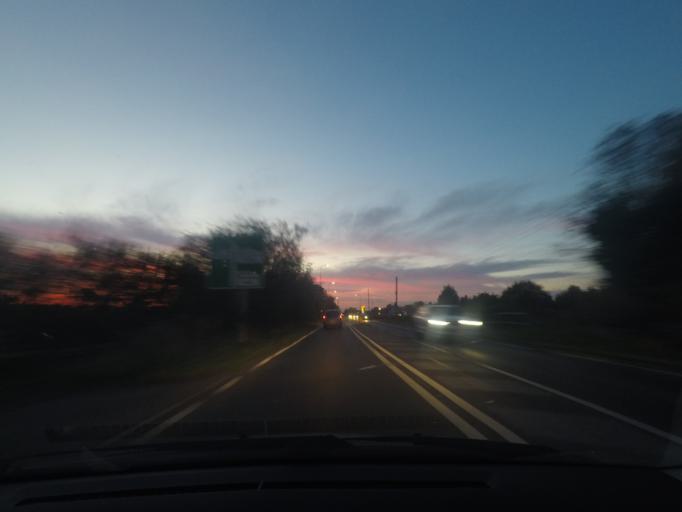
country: GB
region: England
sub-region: East Riding of Yorkshire
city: Thornton
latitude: 53.9325
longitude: -0.8352
